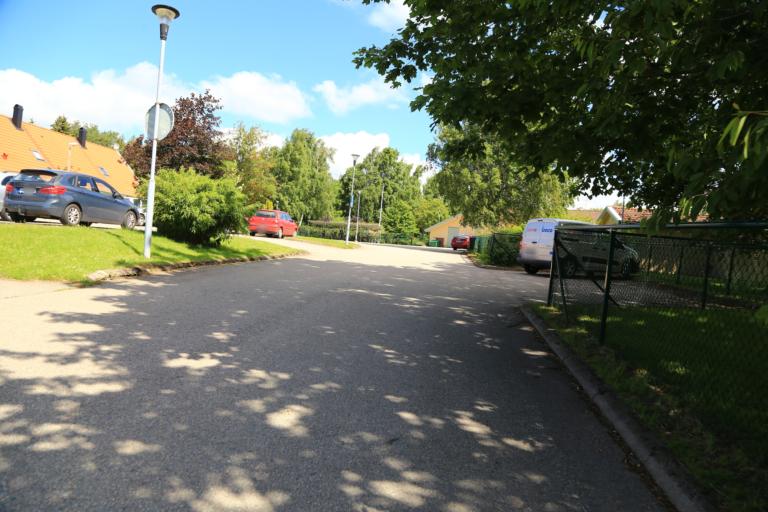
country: SE
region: Halland
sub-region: Varbergs Kommun
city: Varberg
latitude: 57.1149
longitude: 12.2786
